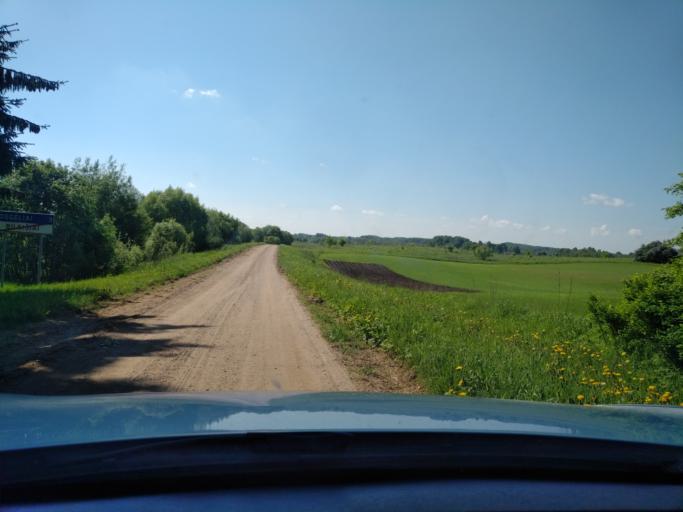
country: LT
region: Panevezys
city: Rokiskis
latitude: 55.7535
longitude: 25.7373
